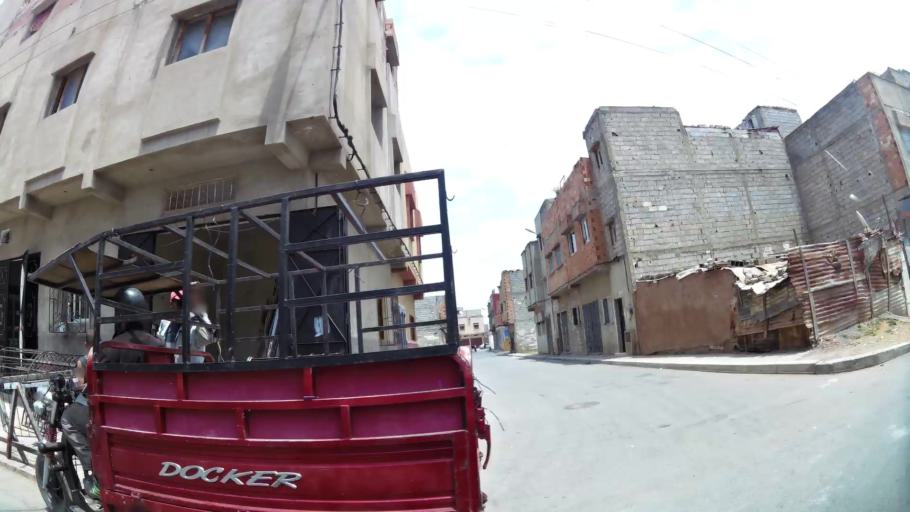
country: MA
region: Rabat-Sale-Zemmour-Zaer
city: Sale
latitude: 34.0679
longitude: -6.7710
